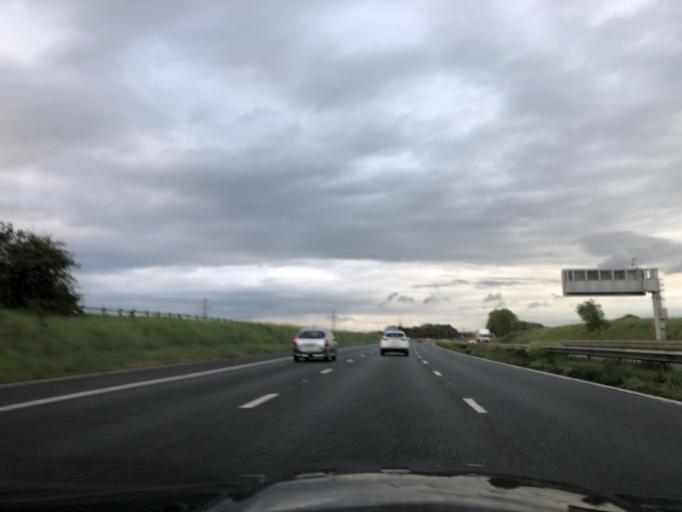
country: GB
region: England
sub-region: Cheshire West and Chester
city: Elton
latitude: 53.2595
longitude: -2.8241
